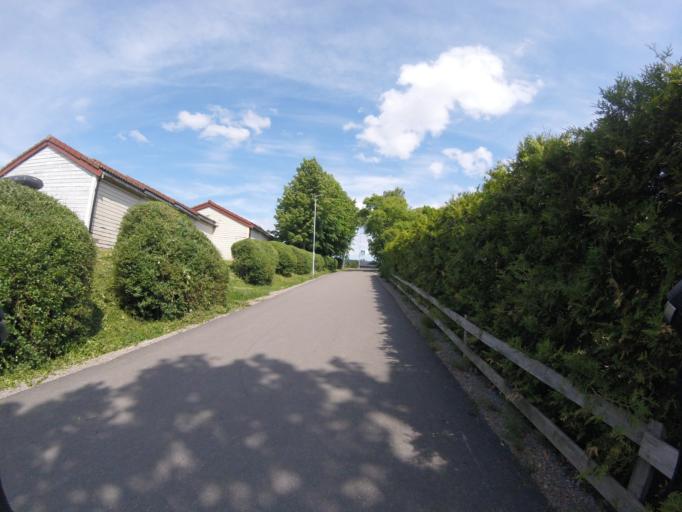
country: NO
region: Akershus
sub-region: Skedsmo
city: Lillestrom
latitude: 59.9910
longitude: 11.0362
